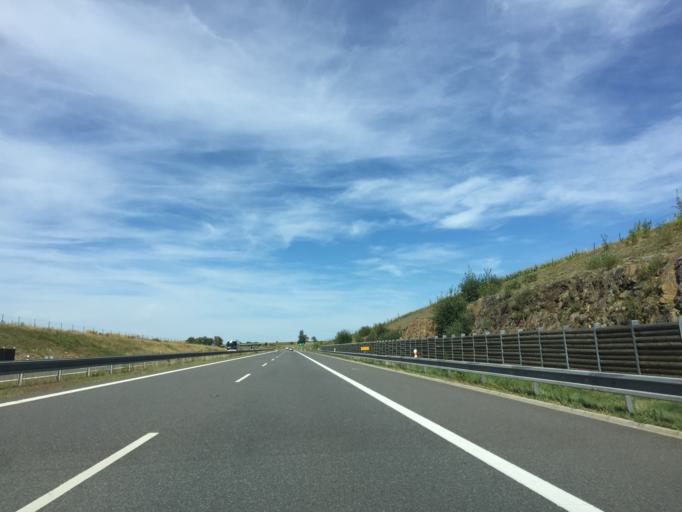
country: CZ
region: Jihocesky
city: Sobeslav
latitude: 49.2512
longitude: 14.7329
